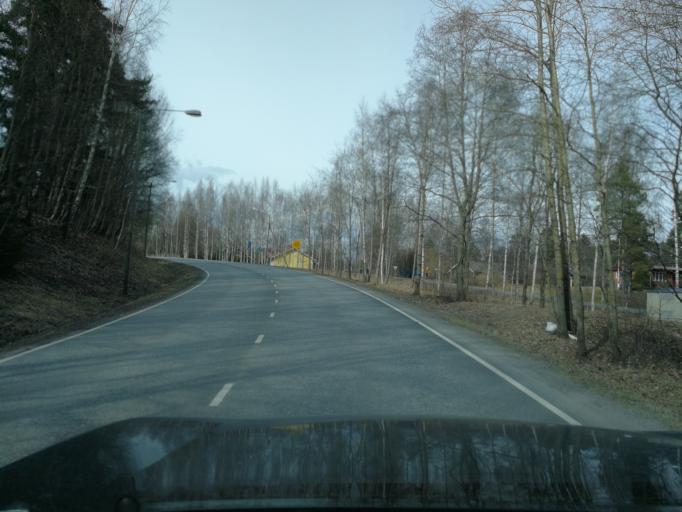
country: FI
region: Uusimaa
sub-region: Helsinki
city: Siuntio
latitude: 60.1311
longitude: 24.2325
